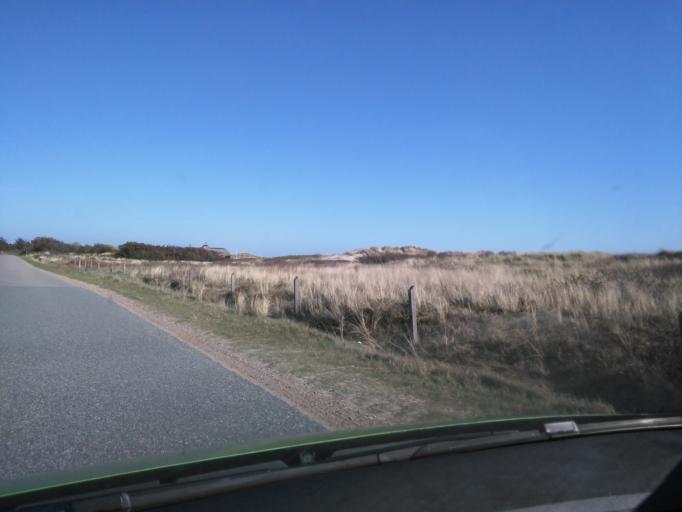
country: DK
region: South Denmark
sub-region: Varde Kommune
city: Oksbol
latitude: 55.5531
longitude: 8.0972
